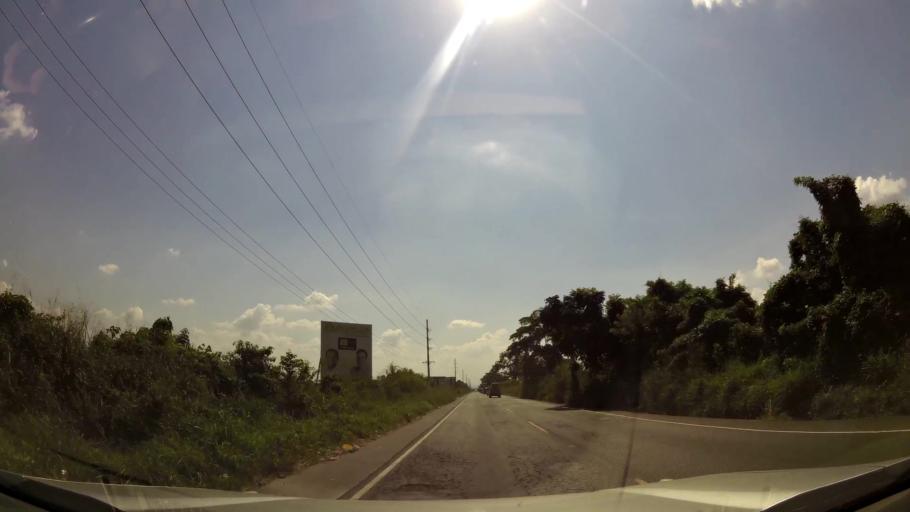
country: GT
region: Suchitepeque
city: Mazatenango
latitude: 14.5415
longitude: -91.5222
